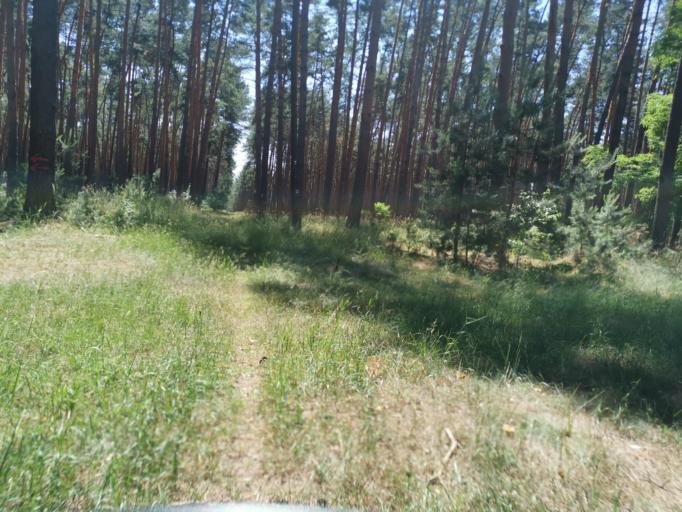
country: CZ
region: South Moravian
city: Bzenec
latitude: 48.9255
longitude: 17.2460
